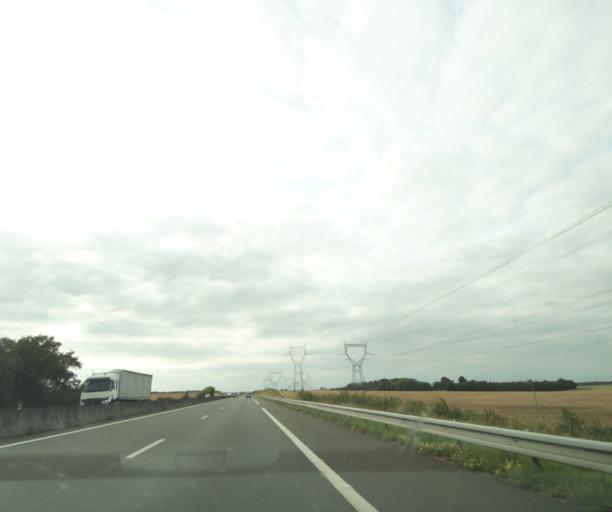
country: FR
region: Centre
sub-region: Departement d'Indre-et-Loire
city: Cerelles
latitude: 47.4908
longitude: 0.6657
